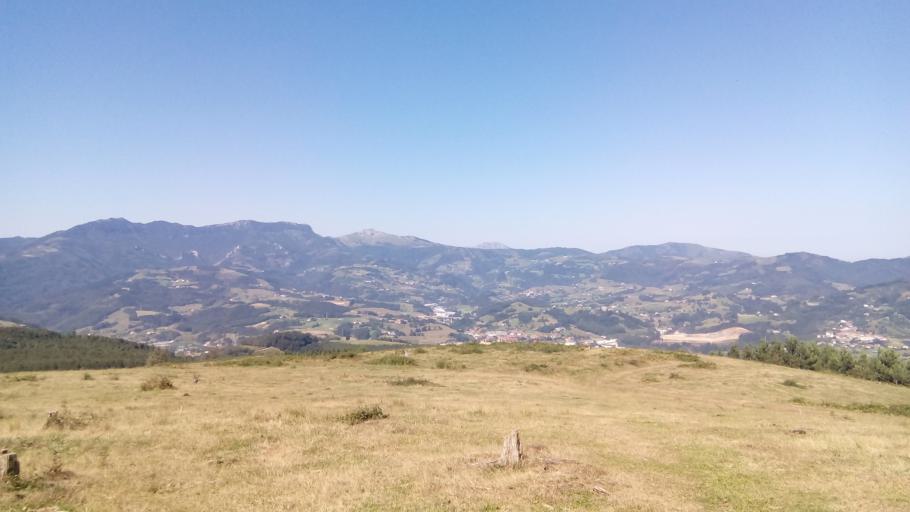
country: ES
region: Basque Country
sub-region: Provincia de Guipuzcoa
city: Andoain
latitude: 43.1895
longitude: -2.0160
